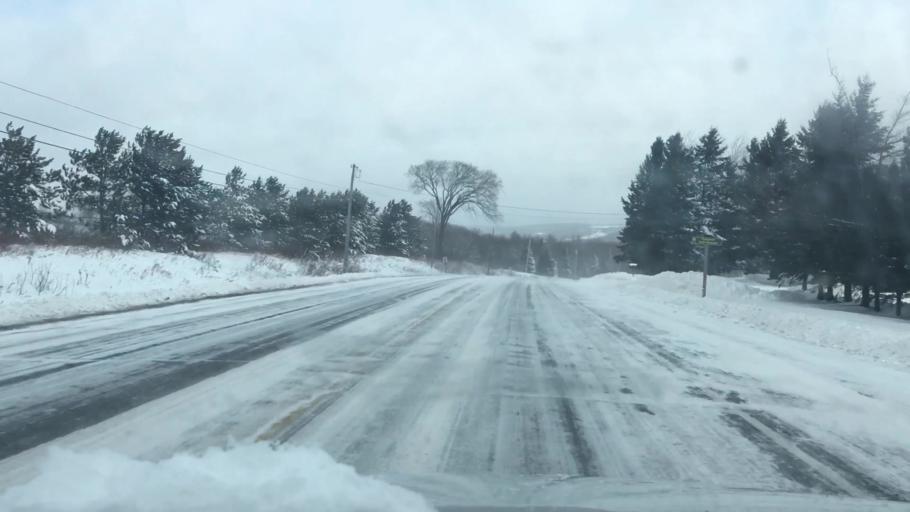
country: US
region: Maine
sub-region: Aroostook County
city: Van Buren
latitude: 47.1380
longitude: -67.9519
